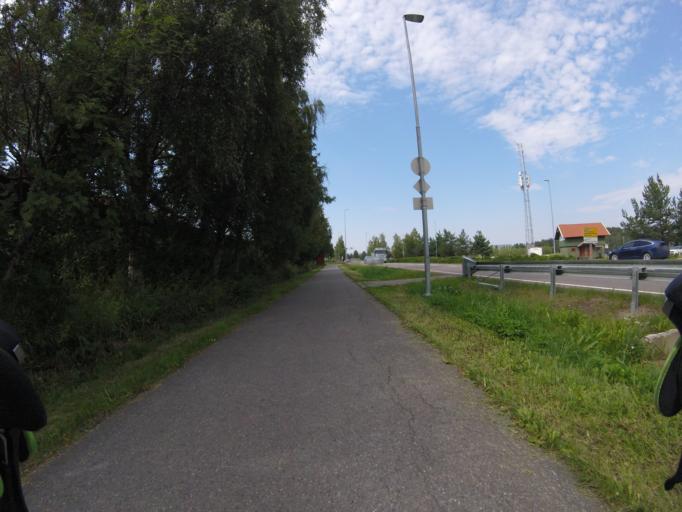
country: NO
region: Akershus
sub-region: Skedsmo
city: Lillestrom
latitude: 59.9553
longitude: 11.0738
